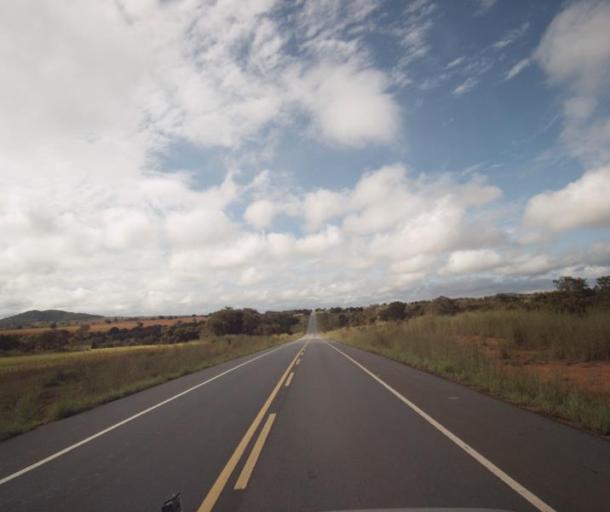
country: BR
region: Goias
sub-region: Barro Alto
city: Barro Alto
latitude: -15.2309
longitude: -48.6939
